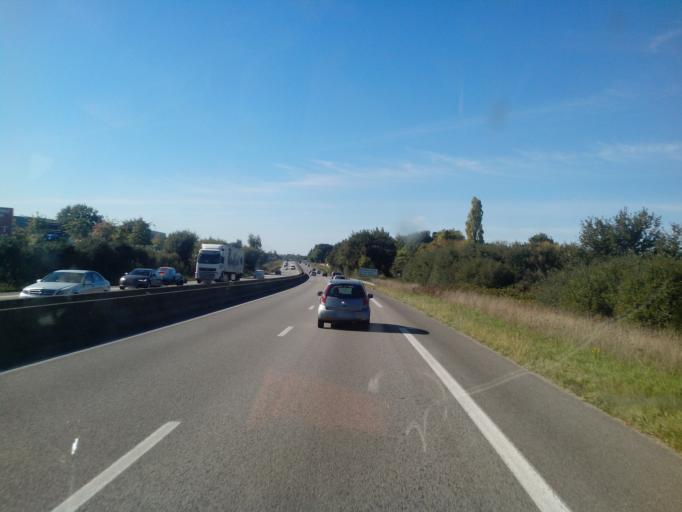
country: FR
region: Brittany
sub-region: Departement du Morbihan
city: Vannes
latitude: 47.6617
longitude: -2.7104
